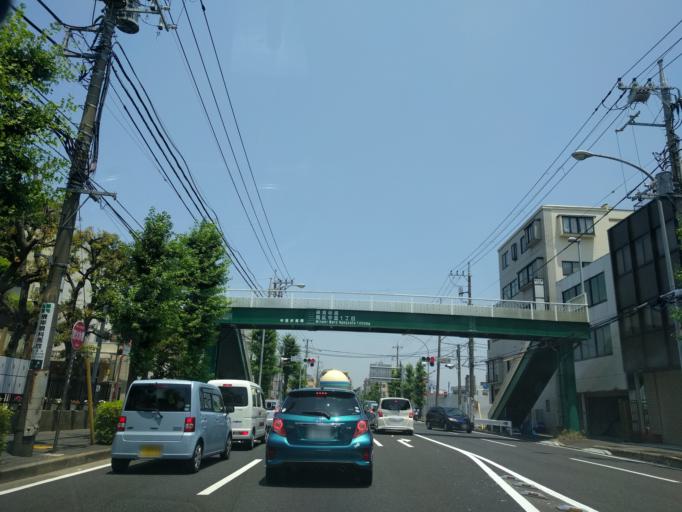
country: JP
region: Kanagawa
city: Yokohama
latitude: 35.4185
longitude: 139.5996
